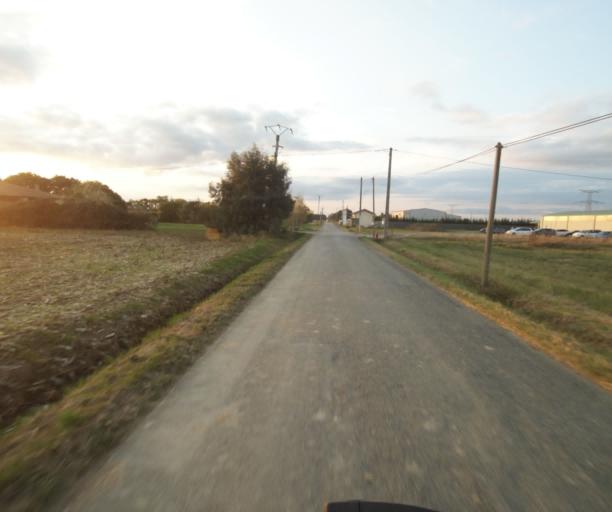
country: FR
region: Midi-Pyrenees
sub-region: Departement du Tarn-et-Garonne
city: Verdun-sur-Garonne
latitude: 43.8217
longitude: 1.2423
